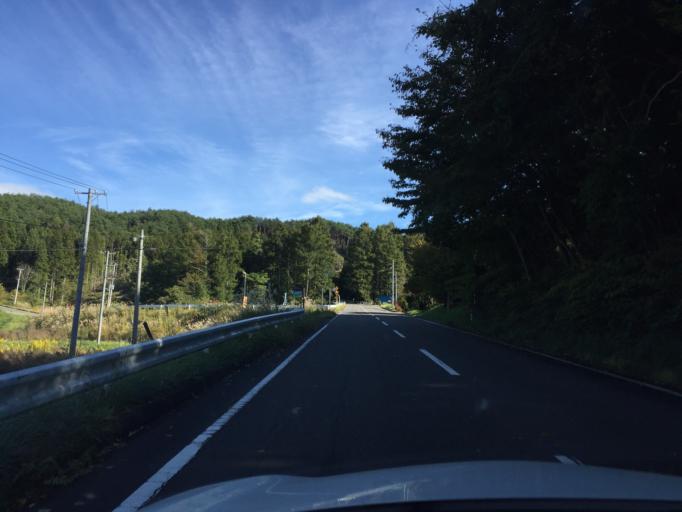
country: JP
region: Fukushima
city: Ishikawa
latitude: 37.1606
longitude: 140.5970
